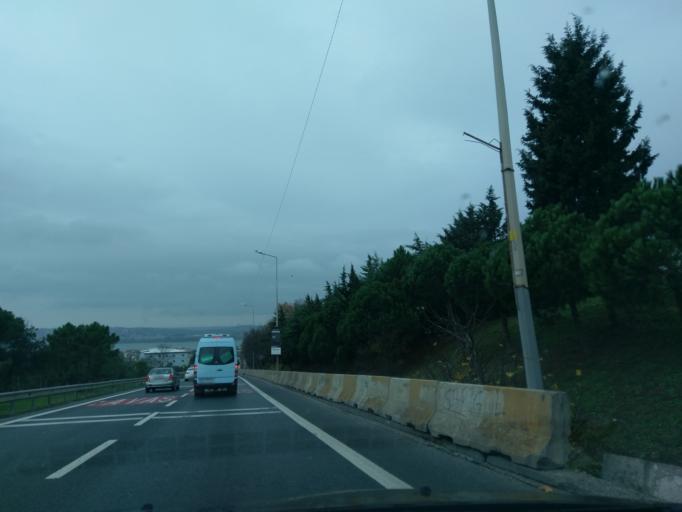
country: TR
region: Istanbul
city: Bueyuekcekmece
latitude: 41.0243
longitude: 28.5955
